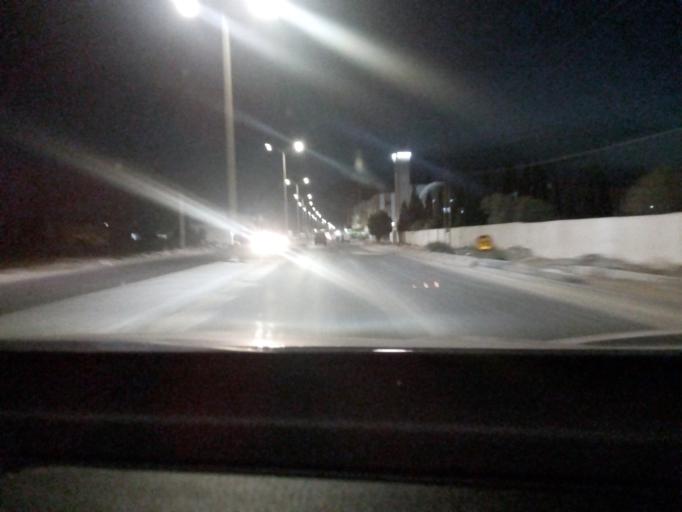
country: TN
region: Safaqis
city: Sfax
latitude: 34.7314
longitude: 10.6712
